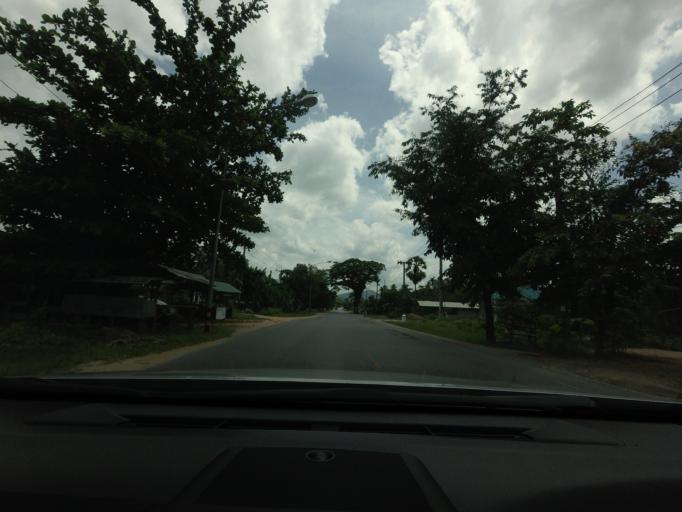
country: TH
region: Yala
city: Raman
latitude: 6.4649
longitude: 101.3823
